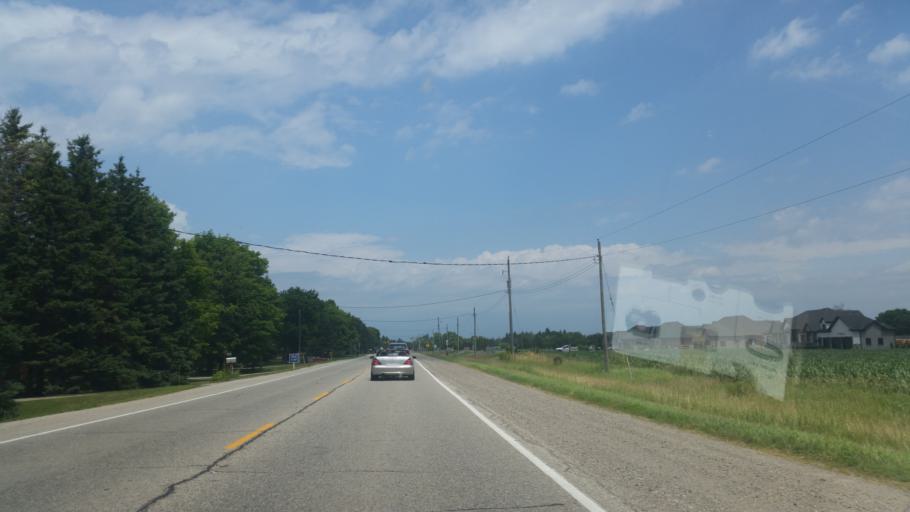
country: CA
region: Ontario
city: Orangeville
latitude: 43.7413
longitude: -80.0809
